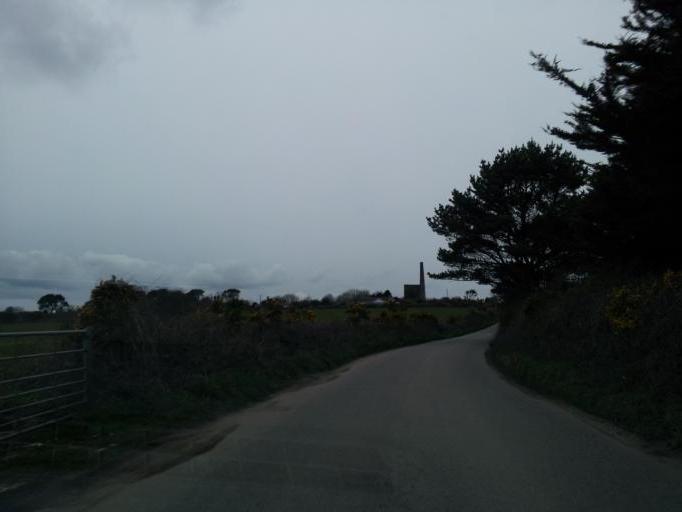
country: GB
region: England
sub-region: Cornwall
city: St. Day
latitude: 50.2597
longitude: -5.1935
